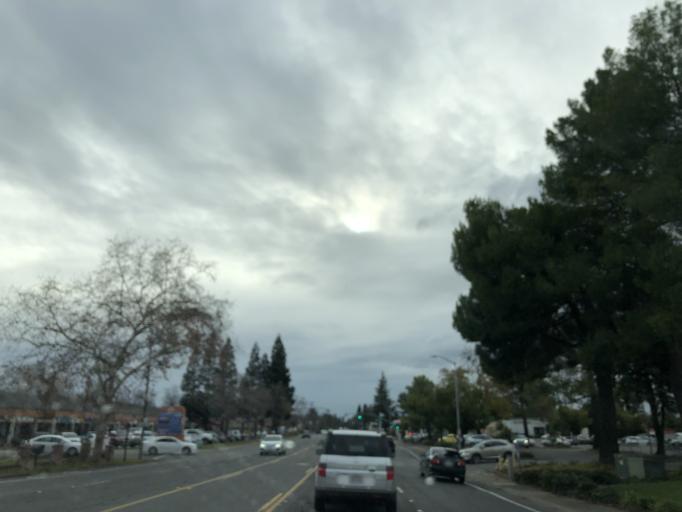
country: US
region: California
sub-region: Sacramento County
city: Carmichael
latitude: 38.5976
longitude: -121.3439
